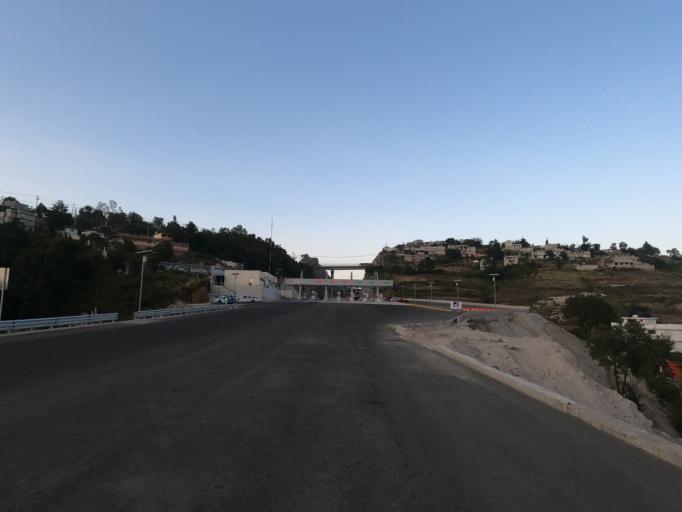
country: MX
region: Mexico
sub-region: Naucalpan de Juarez
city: Ejido el Castillo
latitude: 19.4328
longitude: -99.3040
